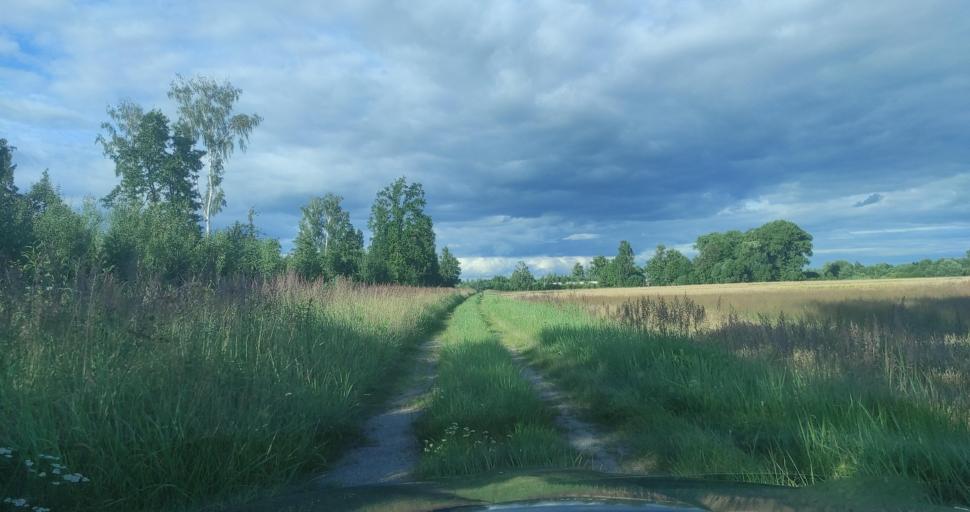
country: LV
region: Dobeles Rajons
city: Dobele
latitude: 56.7051
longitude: 23.4499
